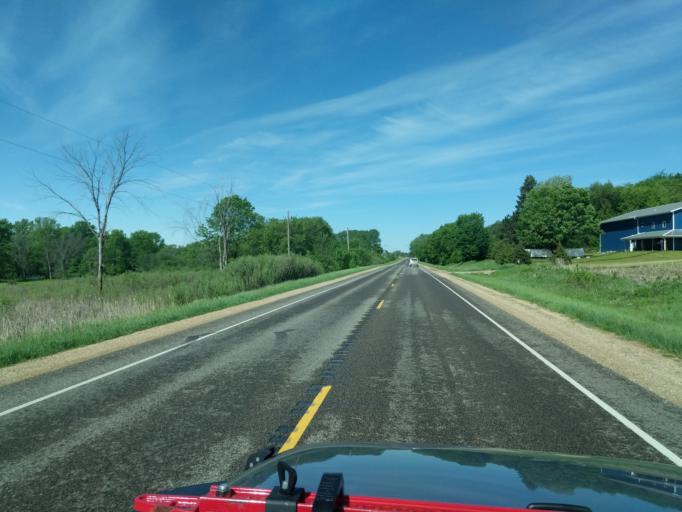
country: US
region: Wisconsin
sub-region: Pierce County
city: River Falls
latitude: 44.8504
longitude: -92.5918
